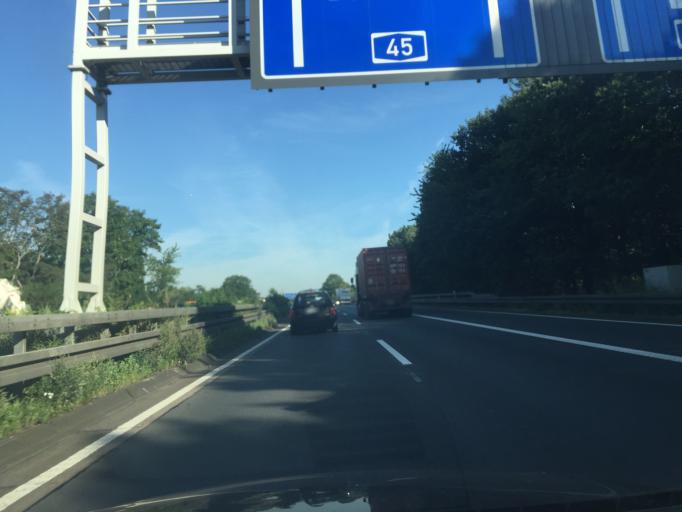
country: DE
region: North Rhine-Westphalia
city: Schwerte
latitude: 51.4261
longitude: 7.5453
